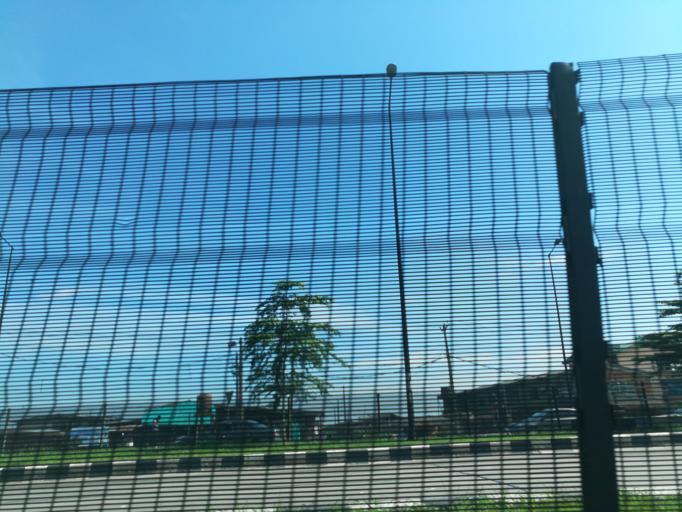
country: NG
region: Lagos
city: Ebute Ikorodu
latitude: 6.6197
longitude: 3.4718
